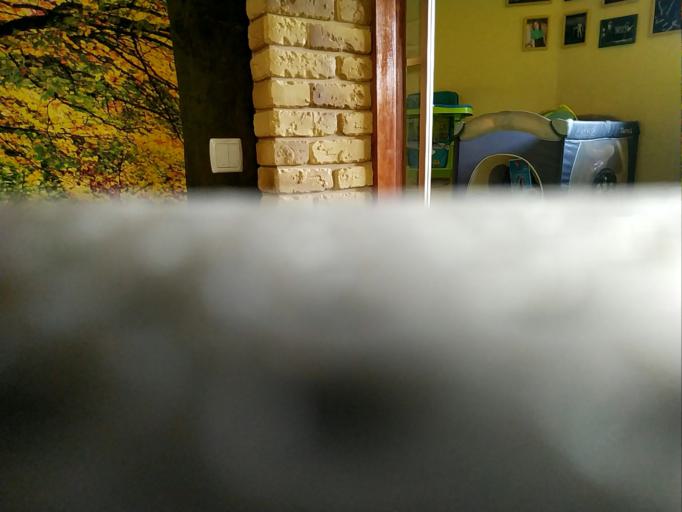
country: RU
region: Kaluga
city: Sukhinichi
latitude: 54.0854
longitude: 35.2850
